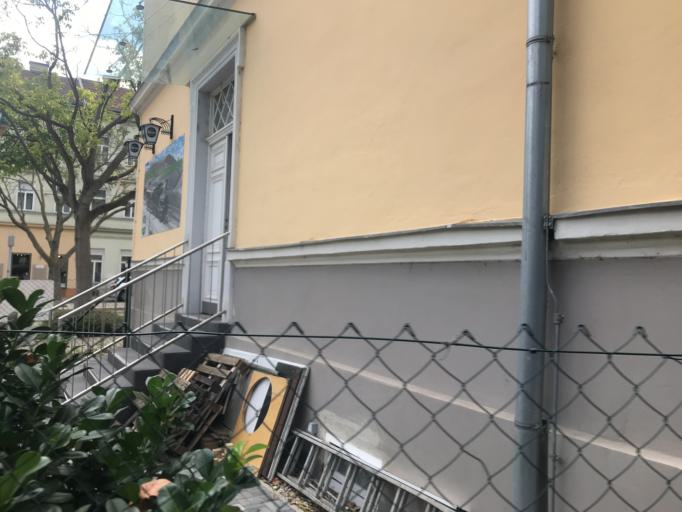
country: AT
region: Lower Austria
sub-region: Politischer Bezirk Korneuburg
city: Langenzersdorf
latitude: 48.2597
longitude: 16.3627
